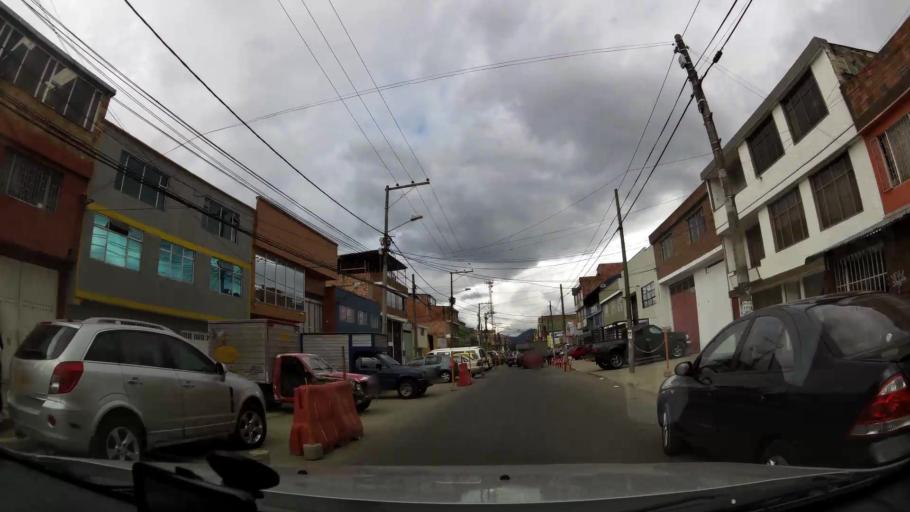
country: CO
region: Bogota D.C.
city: Bogota
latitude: 4.6115
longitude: -74.1361
